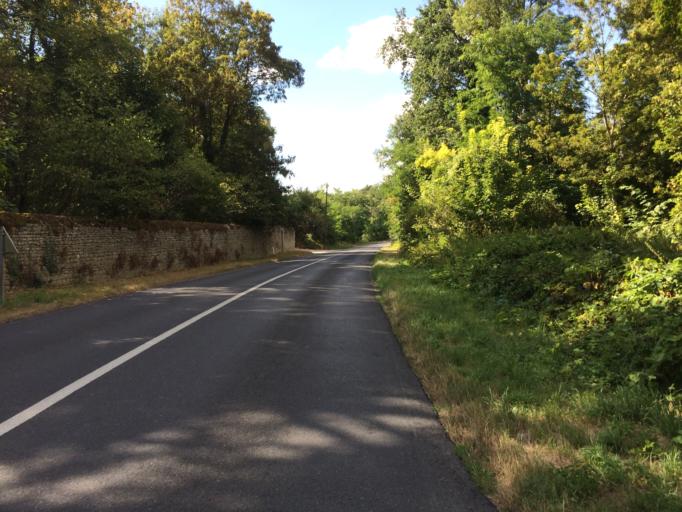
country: FR
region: Ile-de-France
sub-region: Departement de l'Essonne
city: Cerny
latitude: 48.4506
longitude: 2.3439
